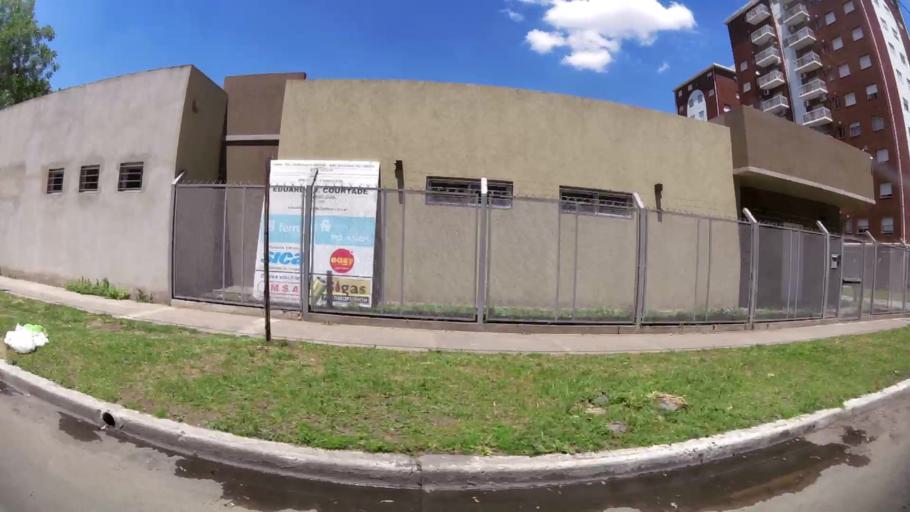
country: AR
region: Buenos Aires
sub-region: Partido de Merlo
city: Merlo
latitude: -34.6632
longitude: -58.7013
